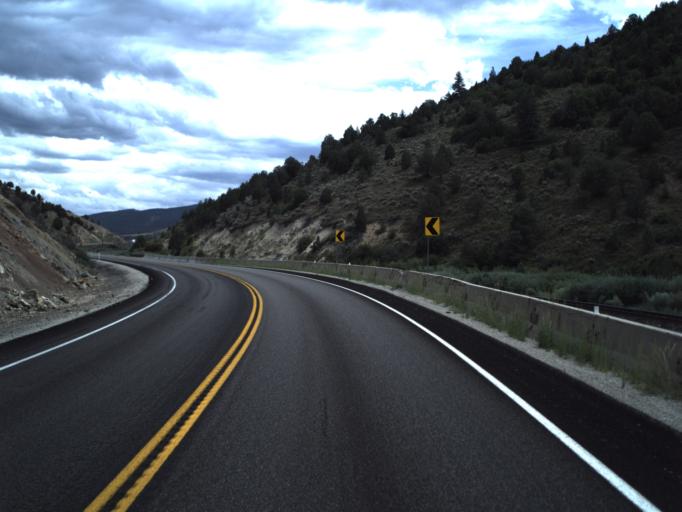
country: US
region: Utah
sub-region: Utah County
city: Mapleton
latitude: 39.9870
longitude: -111.3661
